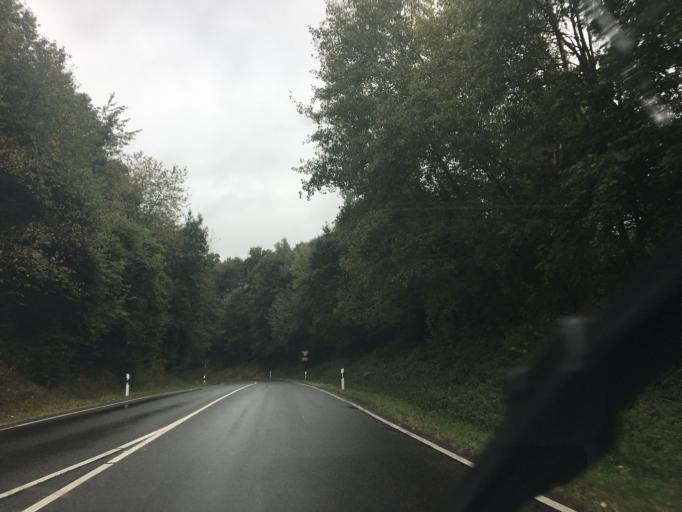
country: DE
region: Rheinland-Pfalz
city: Montabaur
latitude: 50.4361
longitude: 7.8428
